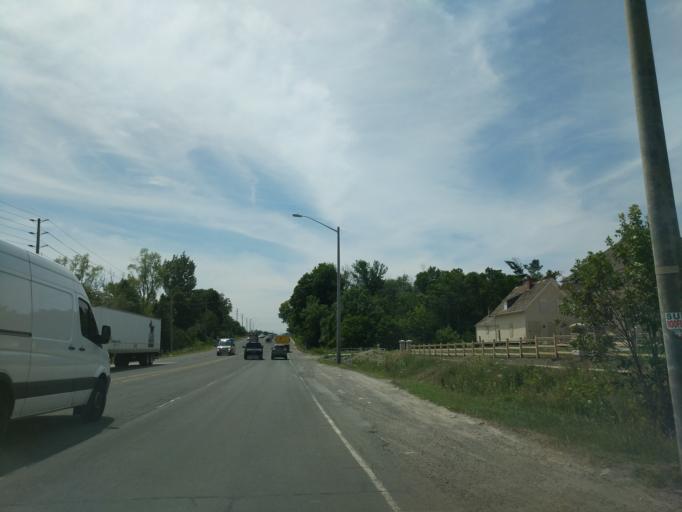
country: CA
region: Ontario
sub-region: York
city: Richmond Hill
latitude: 43.8645
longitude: -79.4703
